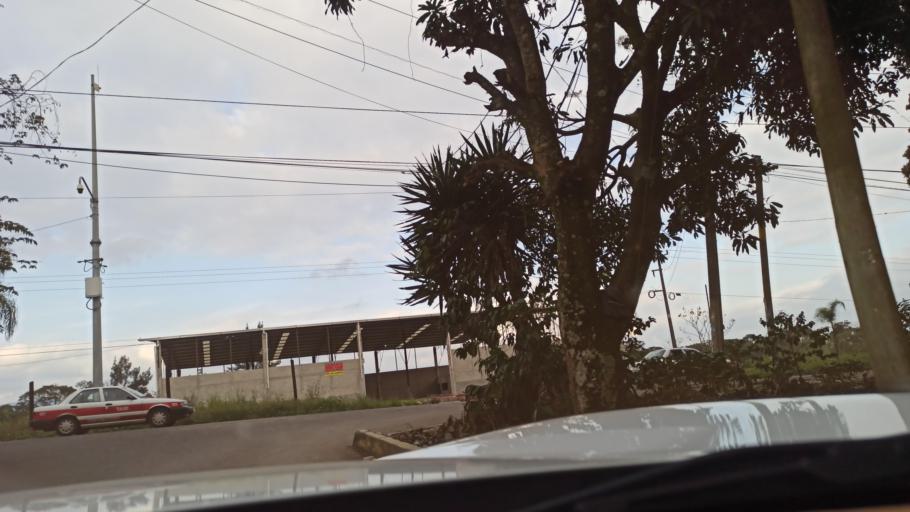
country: MX
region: Veracruz
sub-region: Fortin
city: Monte Salas
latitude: 18.9261
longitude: -97.0107
